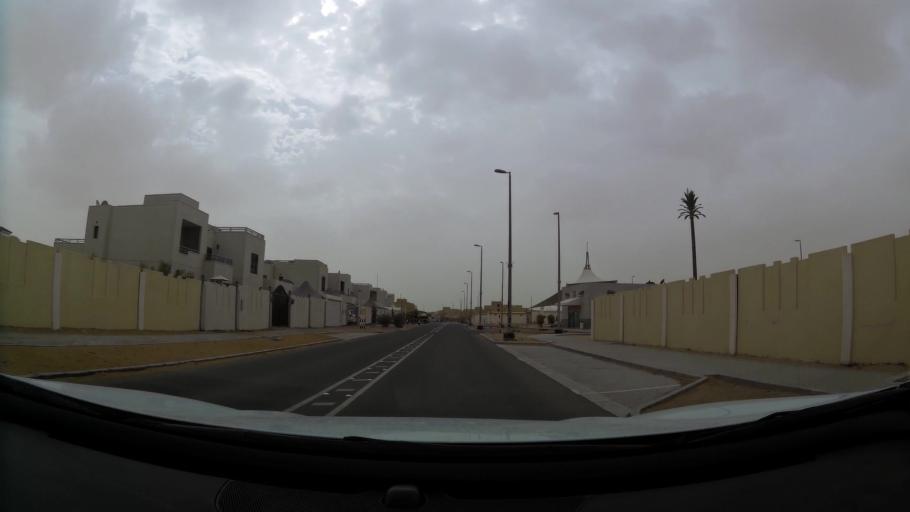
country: AE
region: Abu Dhabi
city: Abu Dhabi
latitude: 24.4575
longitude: 54.7171
